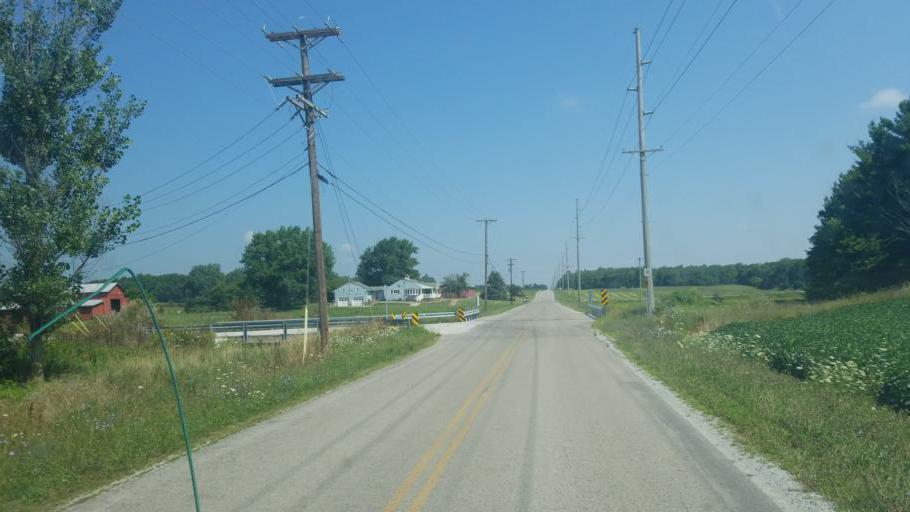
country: US
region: Ohio
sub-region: Hardin County
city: Kenton
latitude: 40.7027
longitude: -83.6536
